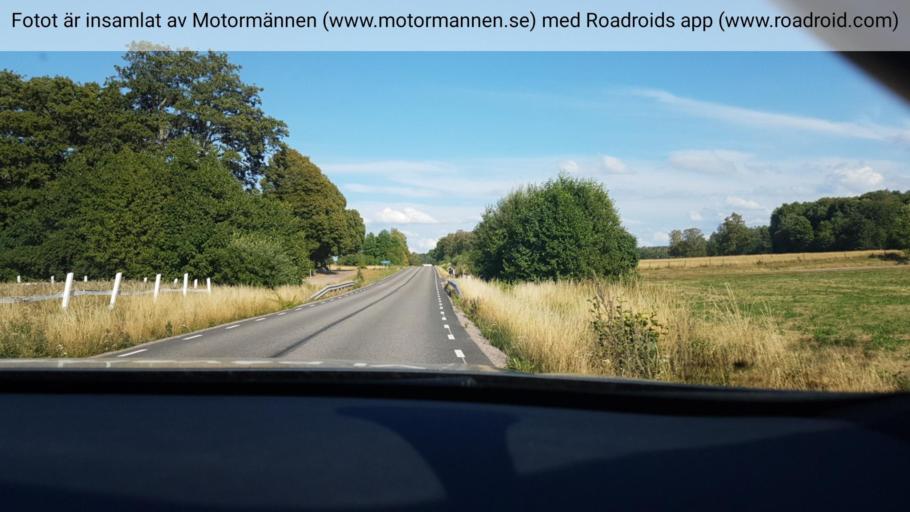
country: SE
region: Vaestra Goetaland
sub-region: Mariestads Kommun
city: Mariestad
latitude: 58.6370
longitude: 13.6549
